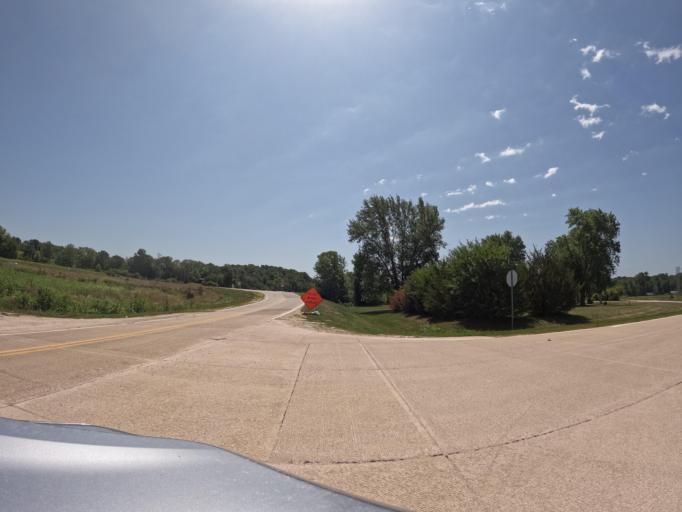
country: US
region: Iowa
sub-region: Henry County
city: Mount Pleasant
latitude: 40.9020
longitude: -91.5566
